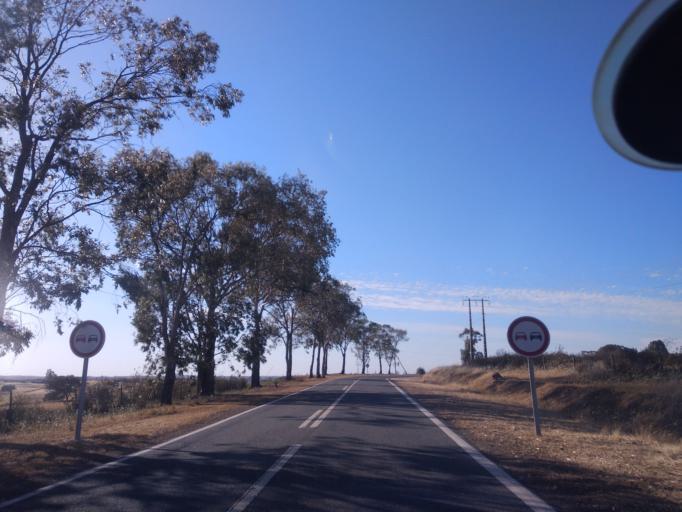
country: PT
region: Beja
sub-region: Almodovar
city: Almodovar
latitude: 37.4478
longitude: -7.9966
